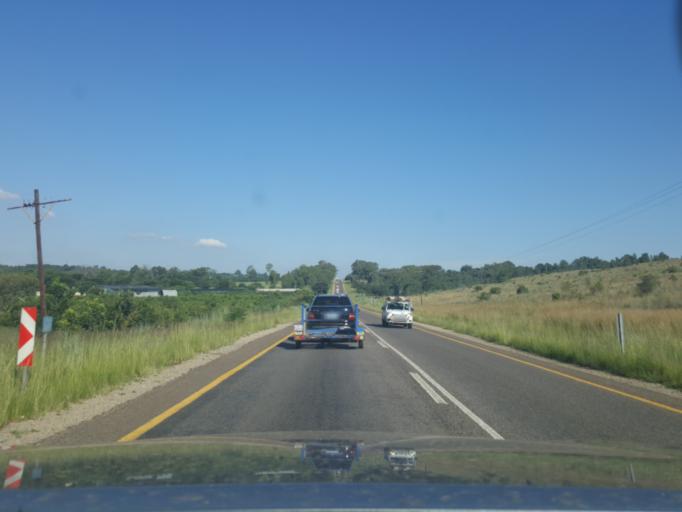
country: ZA
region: Gauteng
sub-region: City of Tshwane Metropolitan Municipality
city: Cullinan
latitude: -25.7771
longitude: 28.4903
